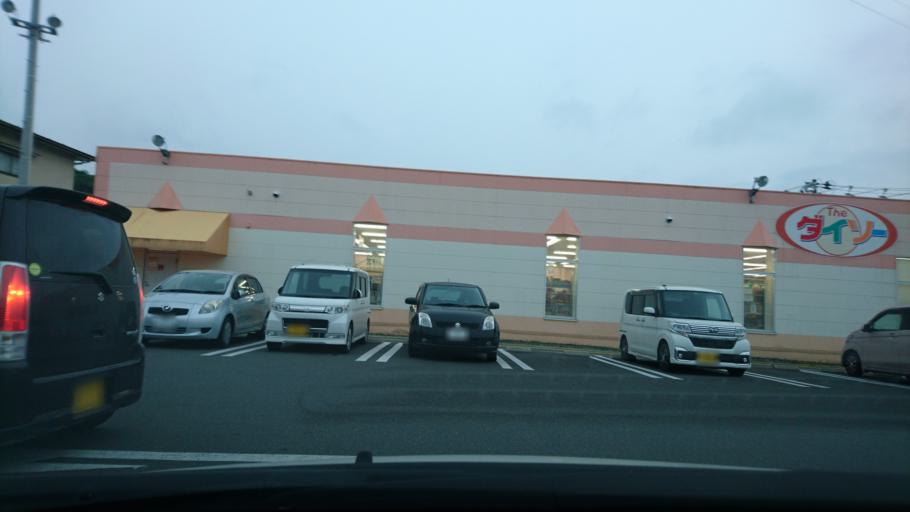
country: JP
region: Iwate
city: Ichinoseki
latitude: 38.9246
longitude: 141.1456
